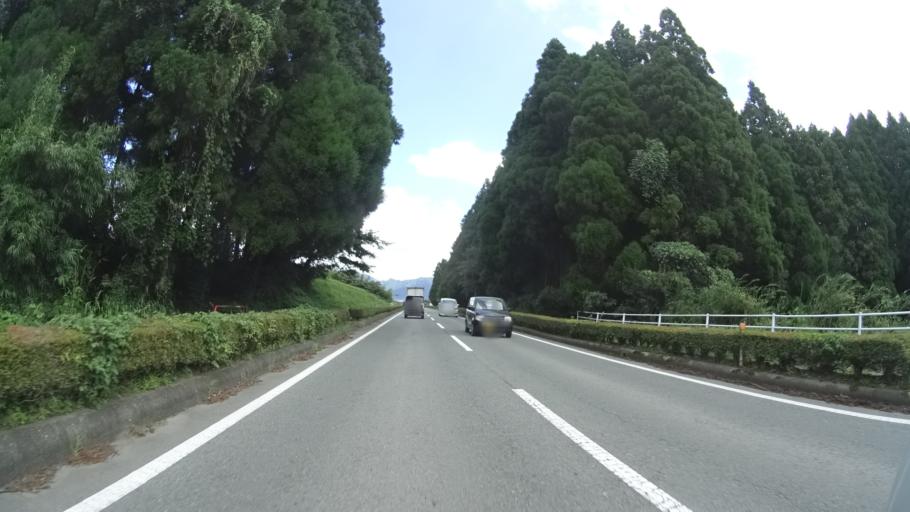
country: JP
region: Kumamoto
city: Aso
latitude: 32.8306
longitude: 131.0861
